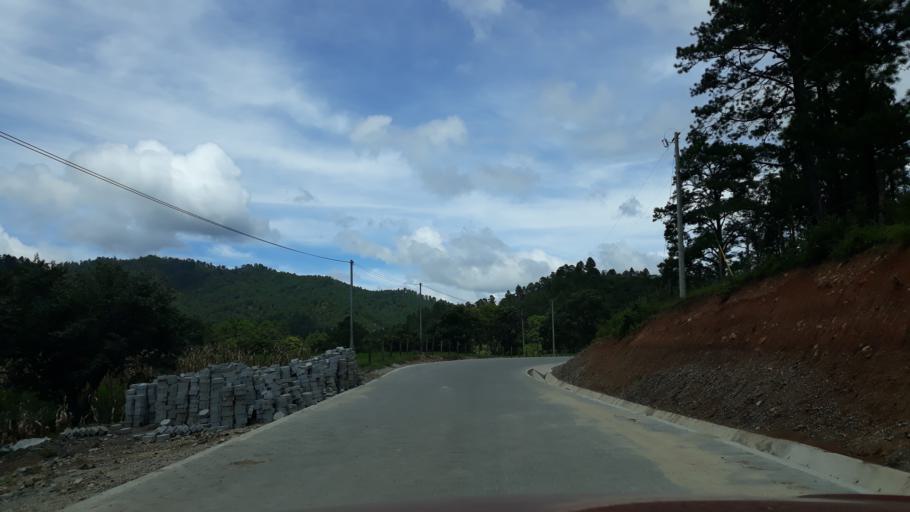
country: HN
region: El Paraiso
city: Santa Cruz
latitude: 13.7382
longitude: -86.6259
